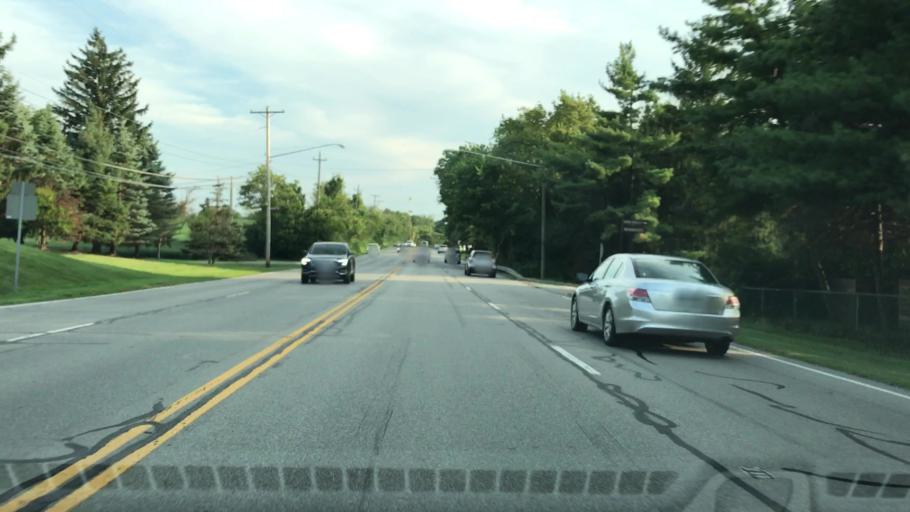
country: US
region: Ohio
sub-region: Franklin County
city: Dublin
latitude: 40.1148
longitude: -83.1098
